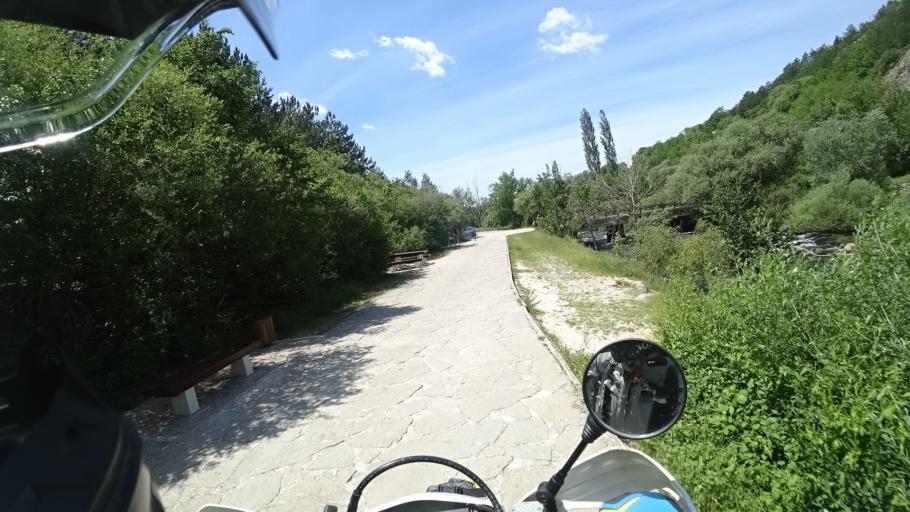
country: HR
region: Sibensko-Kniniska
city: Knin
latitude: 44.0410
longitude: 16.2335
